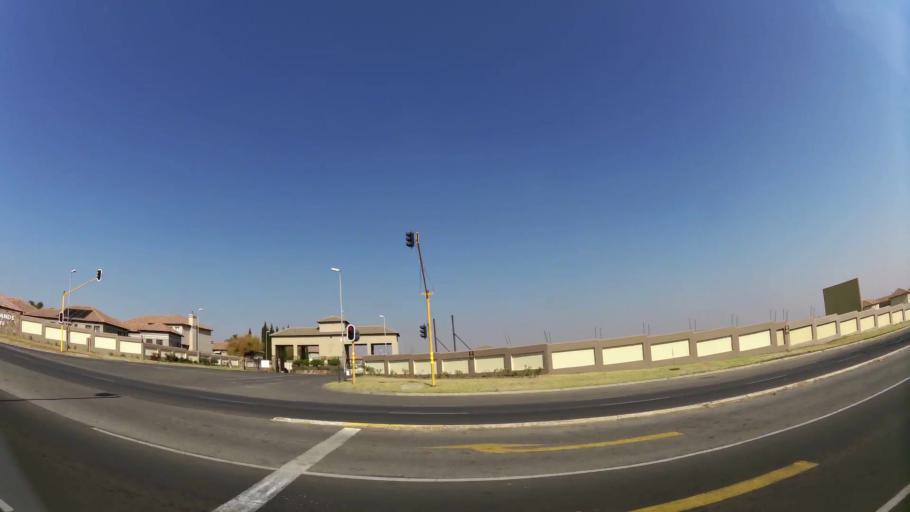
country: ZA
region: Gauteng
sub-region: Ekurhuleni Metropolitan Municipality
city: Boksburg
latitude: -26.2390
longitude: 28.2884
